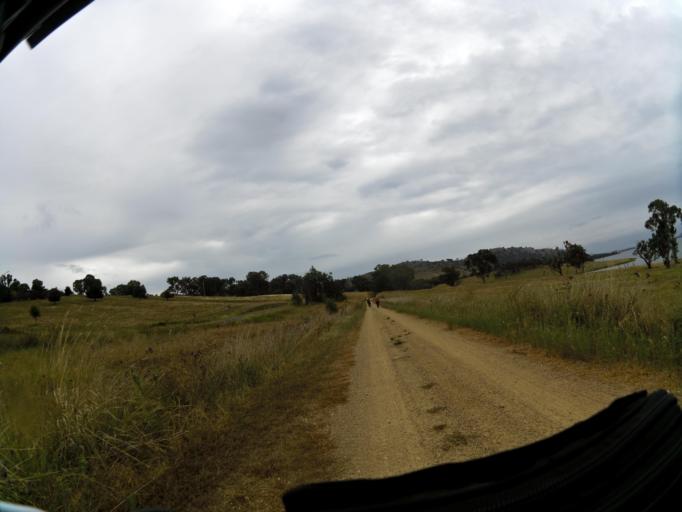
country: AU
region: New South Wales
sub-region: Albury Municipality
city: East Albury
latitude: -36.2017
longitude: 147.0472
